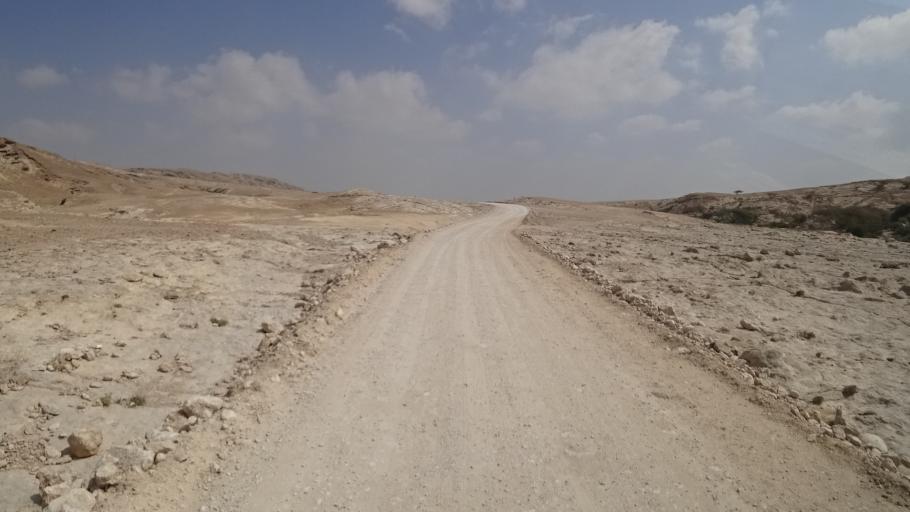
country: OM
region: Zufar
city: Salalah
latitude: 17.2416
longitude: 53.9078
